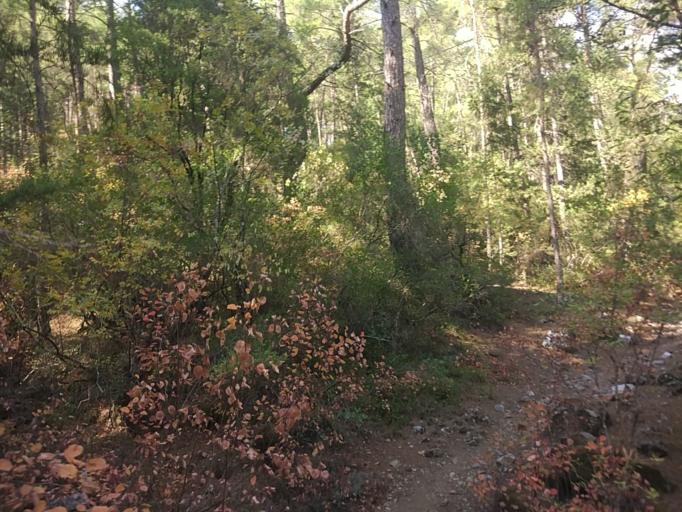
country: TR
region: Antalya
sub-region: Kemer
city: Goeynuek
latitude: 36.6763
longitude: 30.4946
